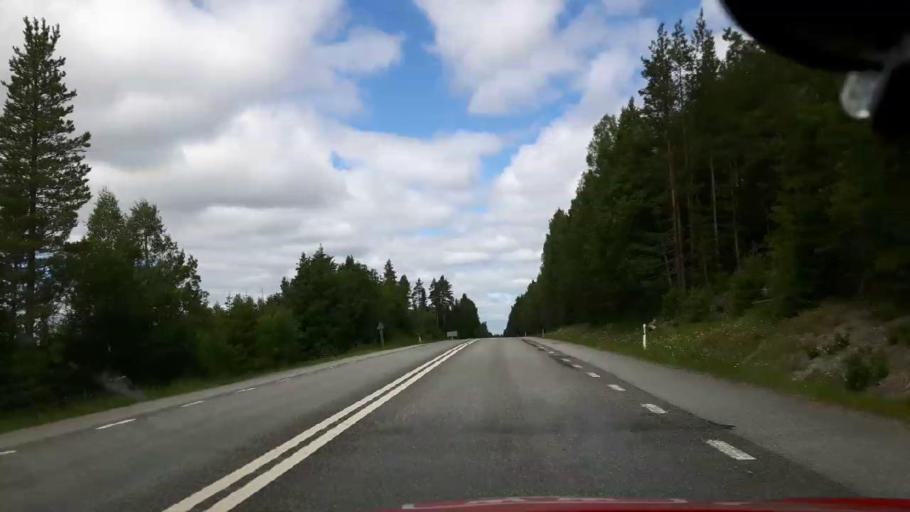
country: SE
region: Jaemtland
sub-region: Braecke Kommun
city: Braecke
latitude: 62.7192
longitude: 15.4532
